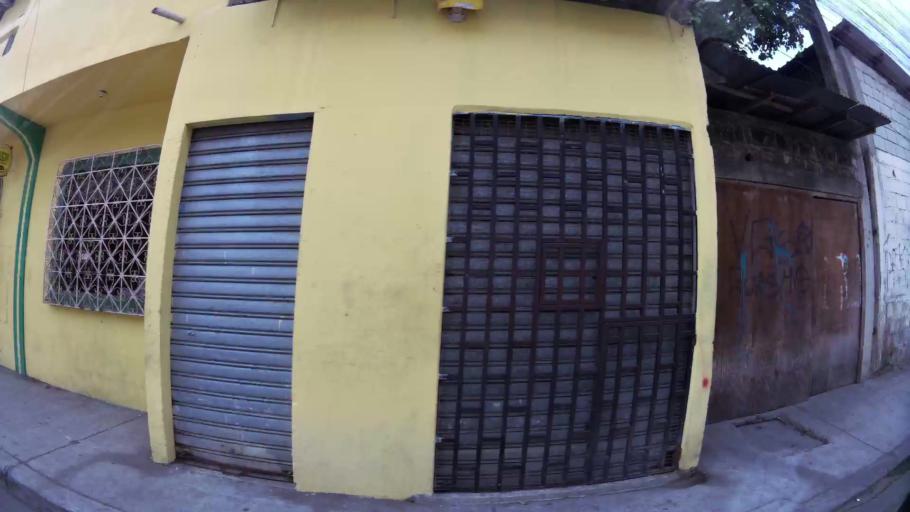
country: EC
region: Guayas
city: Guayaquil
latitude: -2.2605
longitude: -79.9021
